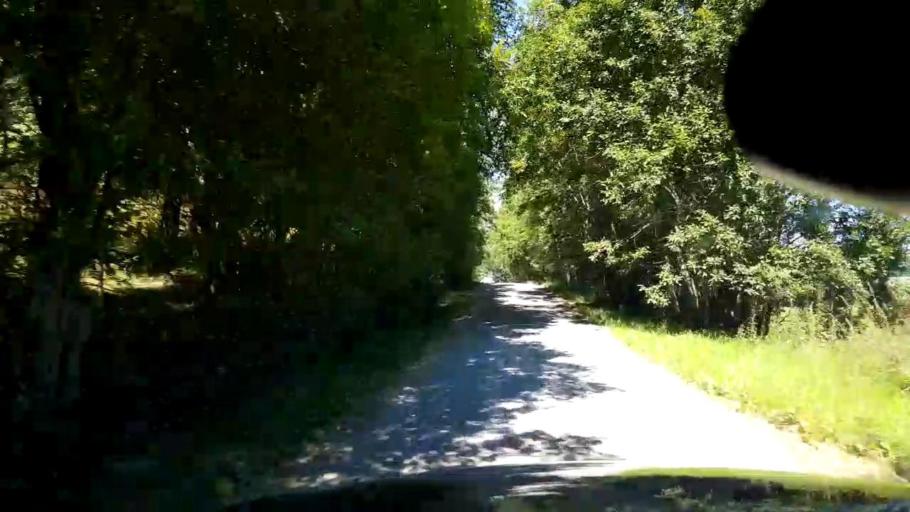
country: SE
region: Uppsala
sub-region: Habo Kommun
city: Balsta
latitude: 59.6177
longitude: 17.6132
